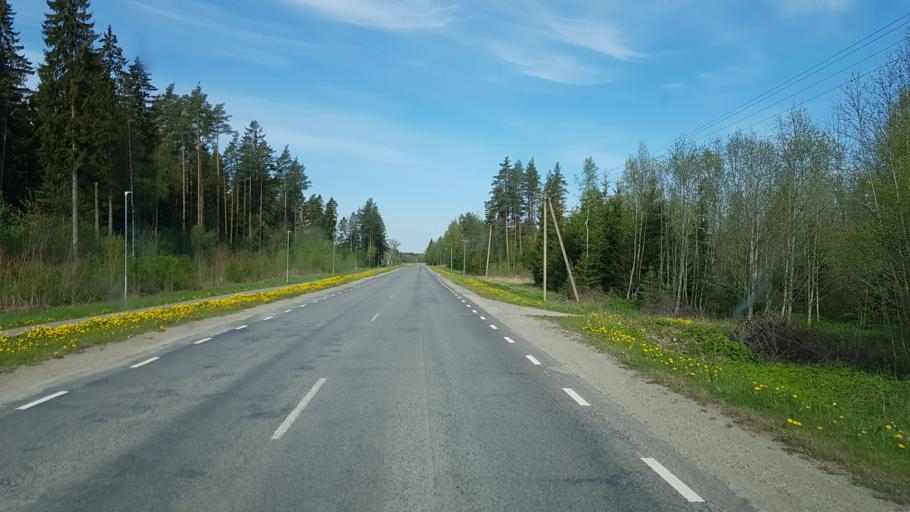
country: EE
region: Ida-Virumaa
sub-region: Kivioli linn
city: Kivioli
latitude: 59.3402
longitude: 26.9968
